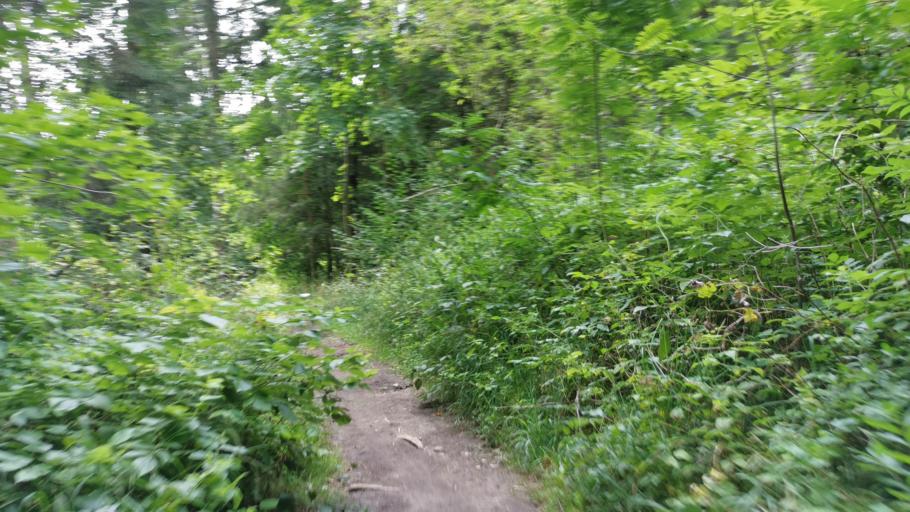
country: DE
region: Bavaria
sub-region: Upper Bavaria
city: Pullach im Isartal
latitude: 48.0851
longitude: 11.5670
